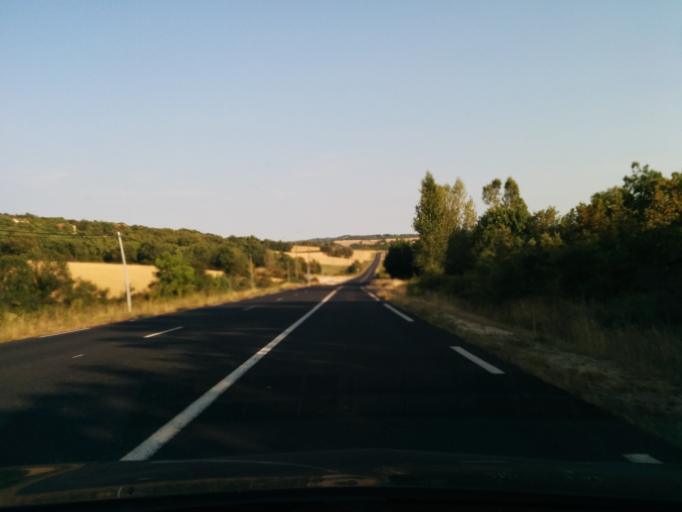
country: FR
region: Midi-Pyrenees
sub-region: Departement du Lot
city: Le Vigan
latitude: 44.7561
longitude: 1.4942
